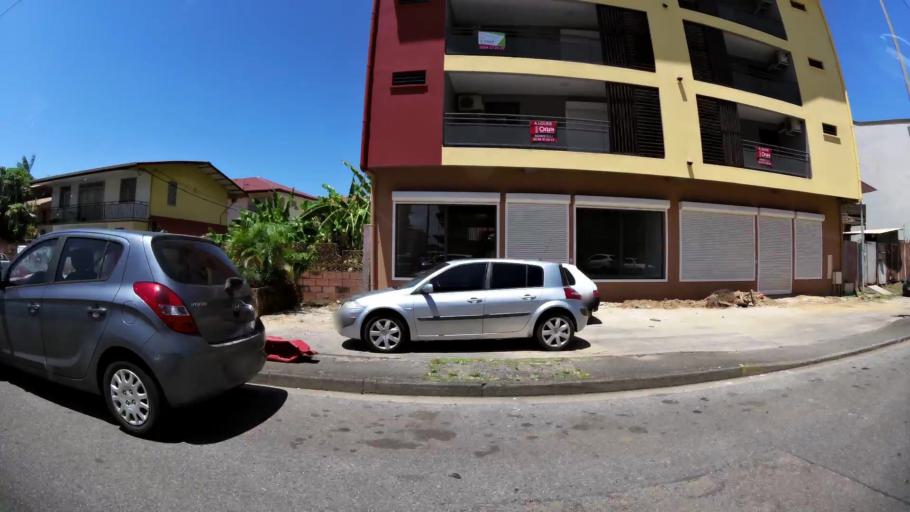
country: GF
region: Guyane
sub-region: Guyane
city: Cayenne
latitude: 4.9339
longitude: -52.3271
